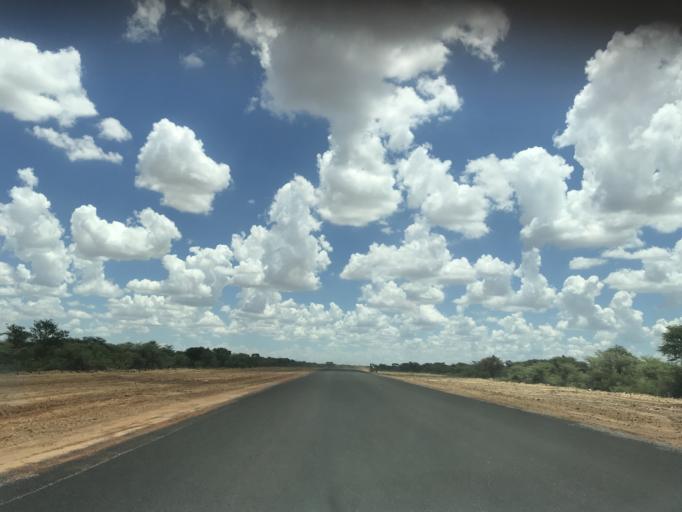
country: BW
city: Mabuli
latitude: -25.8058
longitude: 24.6841
